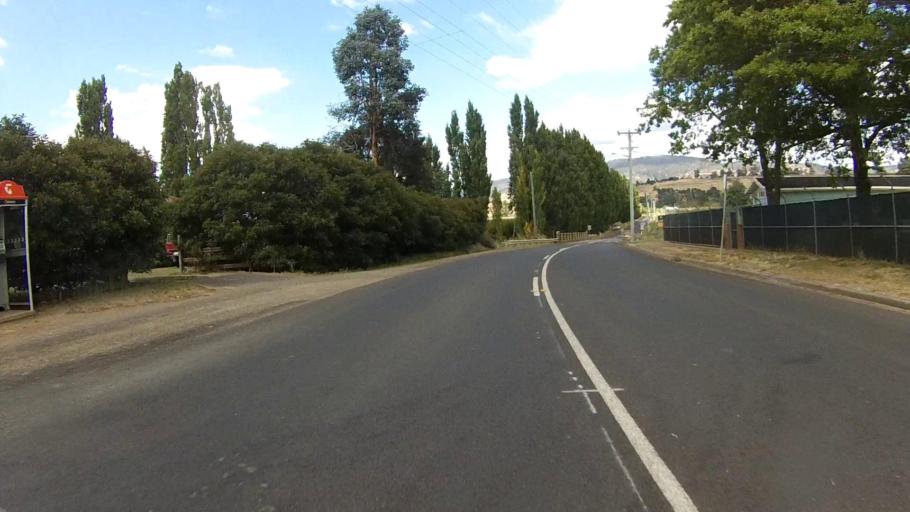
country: AU
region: Tasmania
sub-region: Derwent Valley
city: New Norfolk
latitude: -42.6987
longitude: 146.8907
